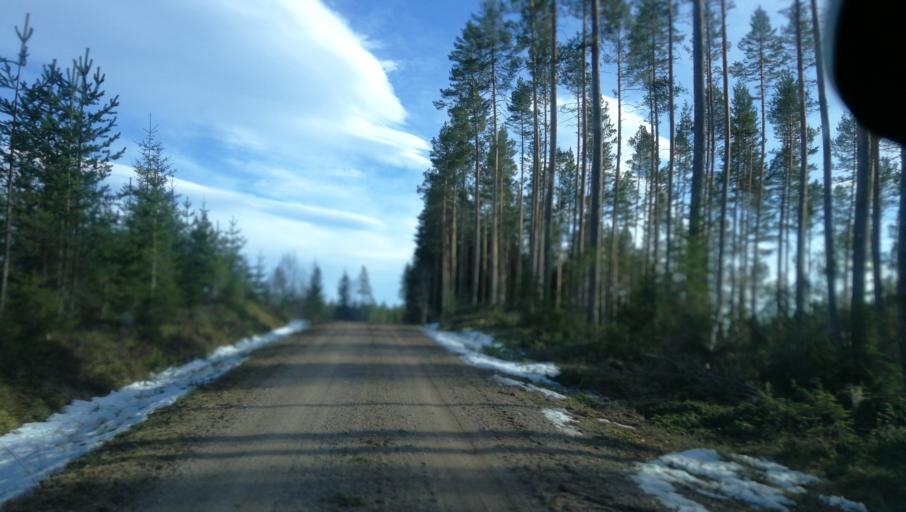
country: SE
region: Dalarna
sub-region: Vansbro Kommun
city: Vansbro
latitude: 60.8114
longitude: 14.2046
